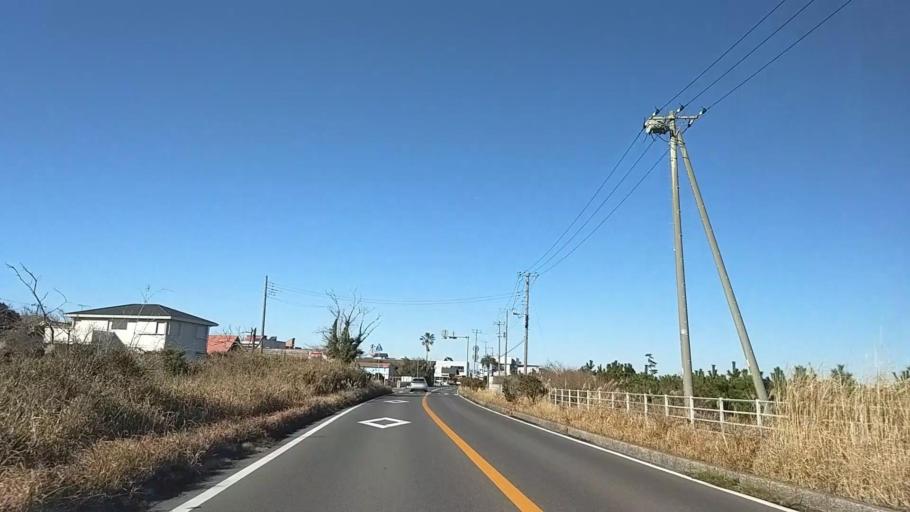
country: JP
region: Chiba
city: Ohara
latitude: 35.3510
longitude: 140.3899
